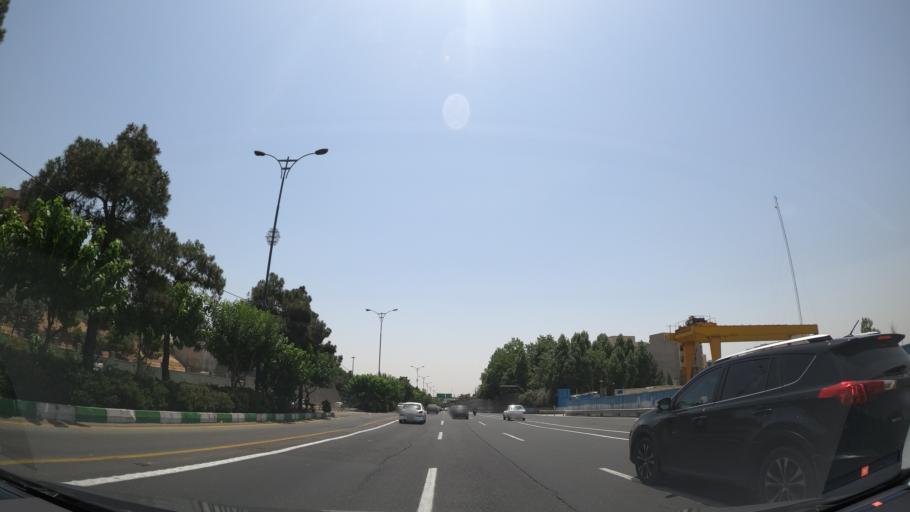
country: IR
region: Tehran
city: Tehran
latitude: 35.7321
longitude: 51.3833
